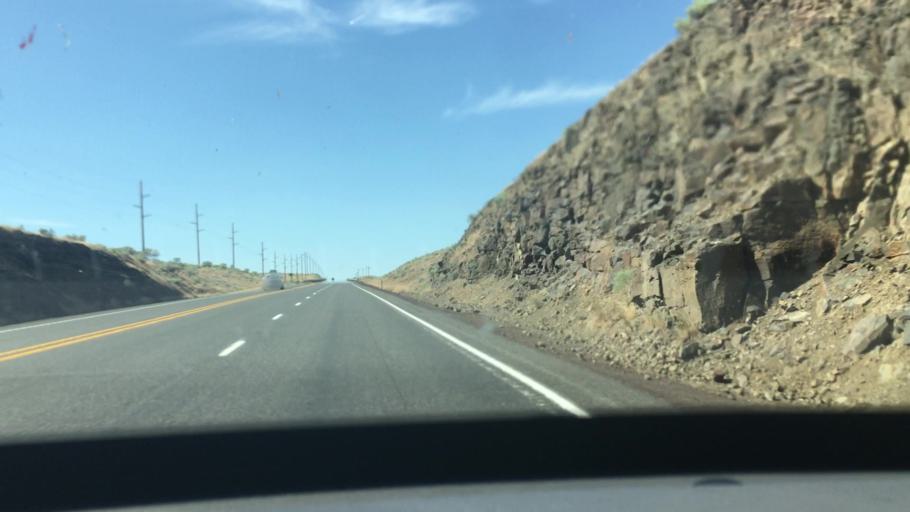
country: US
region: Oregon
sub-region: Sherman County
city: Moro
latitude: 45.5168
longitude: -120.6846
